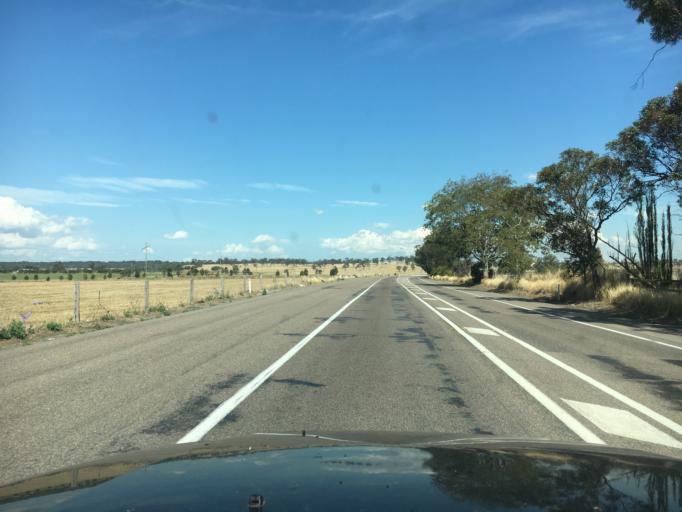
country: AU
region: New South Wales
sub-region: Singleton
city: Singleton
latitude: -32.6186
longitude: 151.2192
